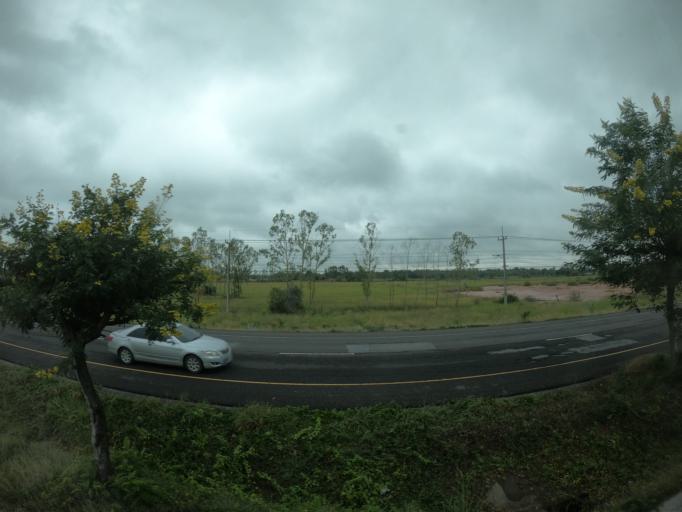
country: TH
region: Nakhon Ratchasima
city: Non Daeng
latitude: 15.4494
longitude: 102.4983
